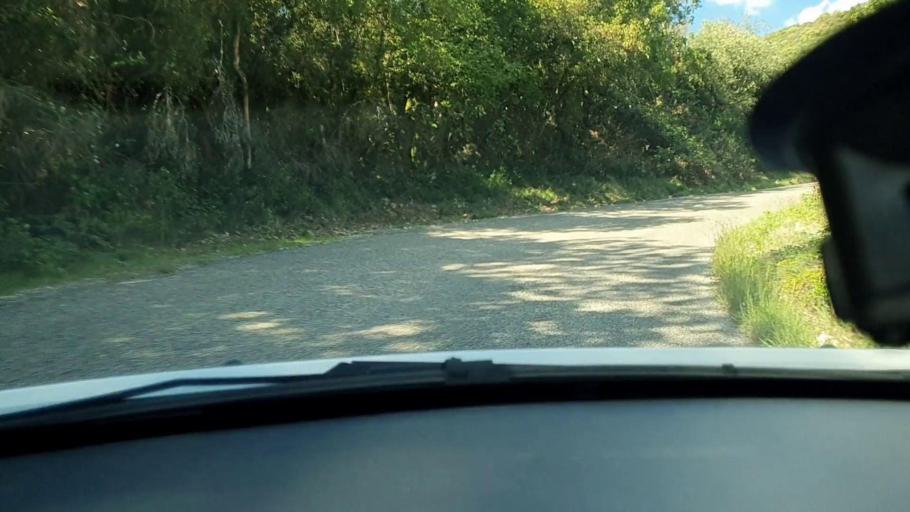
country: FR
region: Languedoc-Roussillon
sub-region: Departement du Gard
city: Goudargues
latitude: 44.1569
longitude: 4.4266
